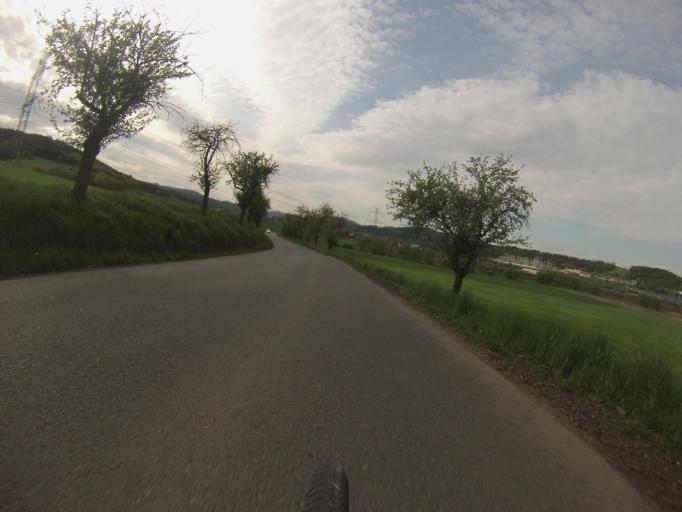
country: CZ
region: South Moravian
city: Cebin
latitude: 49.3198
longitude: 16.4567
